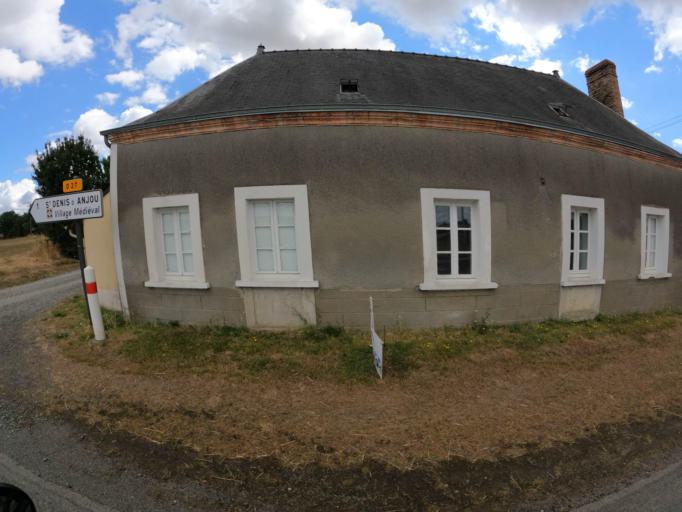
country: FR
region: Pays de la Loire
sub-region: Departement de Maine-et-Loire
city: Mire
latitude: 47.7840
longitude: -0.4562
